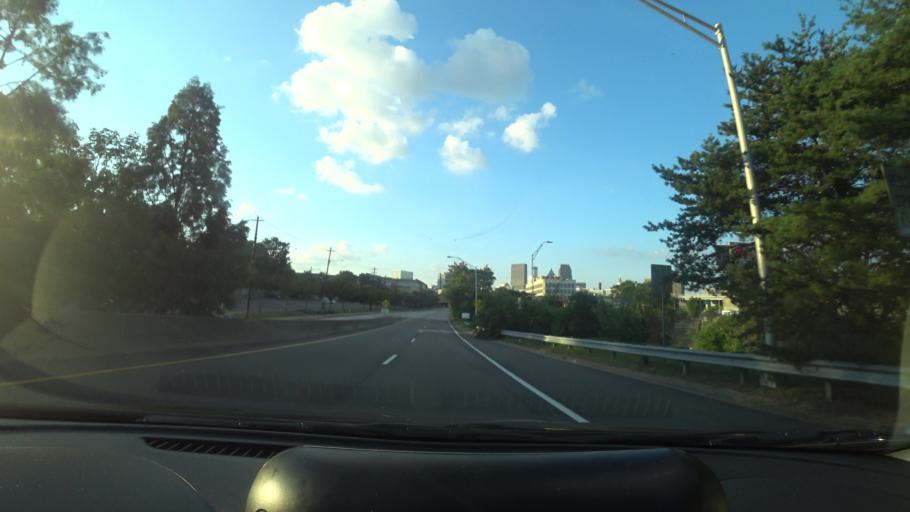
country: US
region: Georgia
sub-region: Fulton County
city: Atlanta
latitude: 33.7392
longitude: -84.3933
